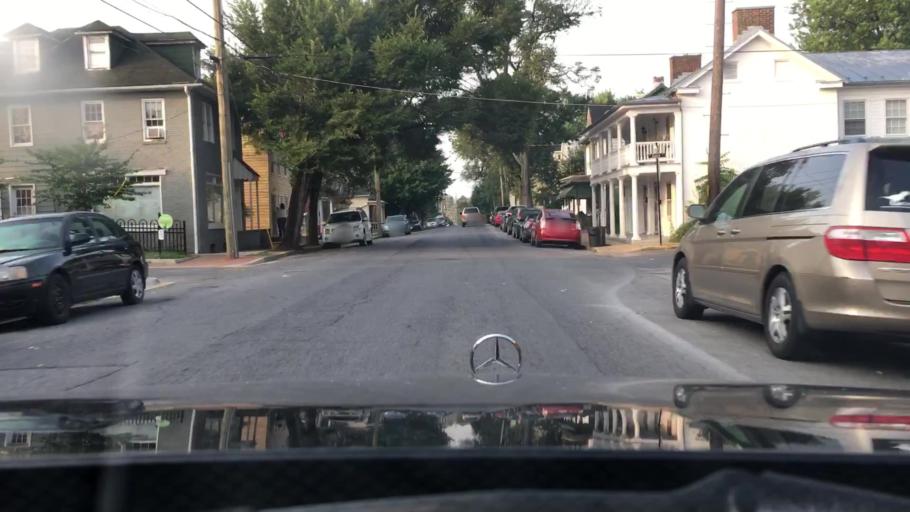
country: US
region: Virginia
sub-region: City of Winchester
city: Winchester
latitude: 39.1800
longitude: -78.1640
